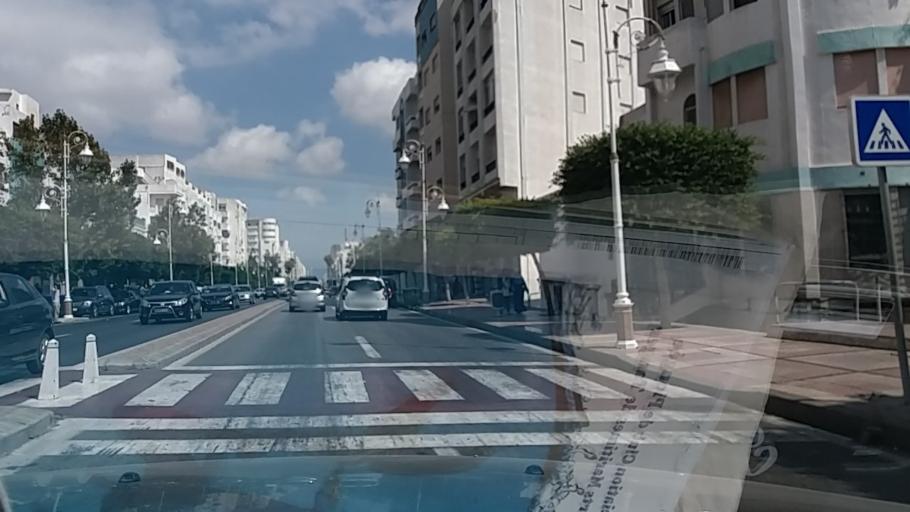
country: MA
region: Tanger-Tetouan
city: Tetouan
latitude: 35.5757
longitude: -5.3591
